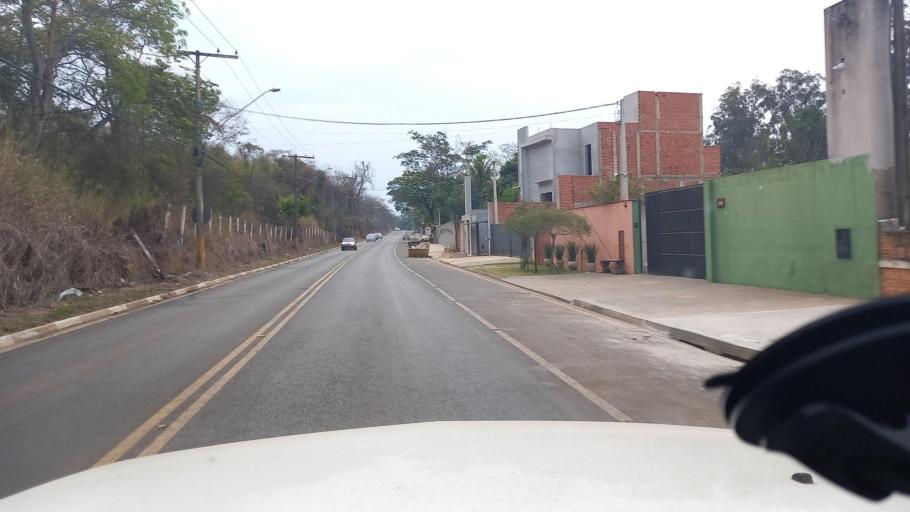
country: BR
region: Sao Paulo
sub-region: Moji-Guacu
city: Mogi-Gaucu
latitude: -22.3778
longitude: -46.9610
